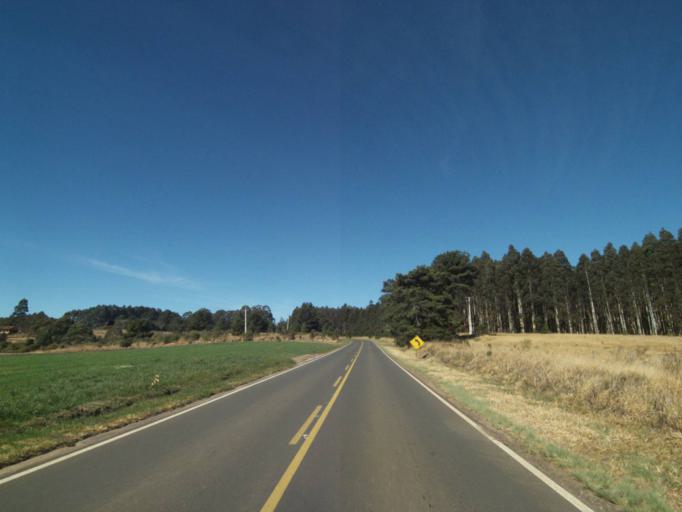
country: BR
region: Parana
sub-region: Tibagi
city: Tibagi
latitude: -24.5952
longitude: -50.2622
